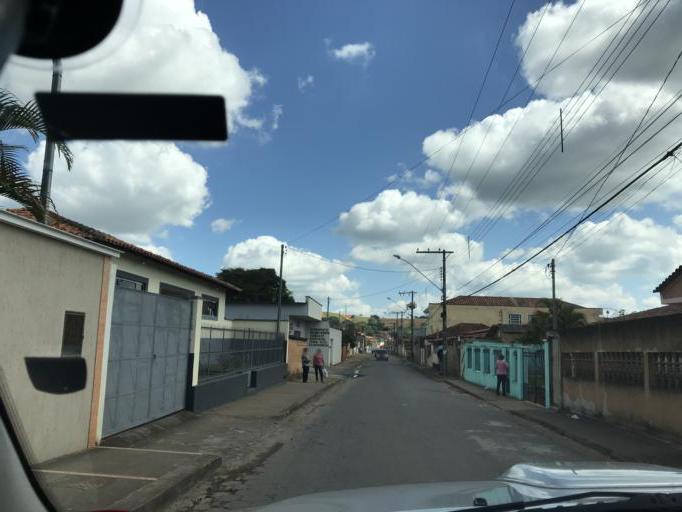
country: BR
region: Minas Gerais
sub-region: Campanha
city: Campanha
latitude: -21.8331
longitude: -45.4031
